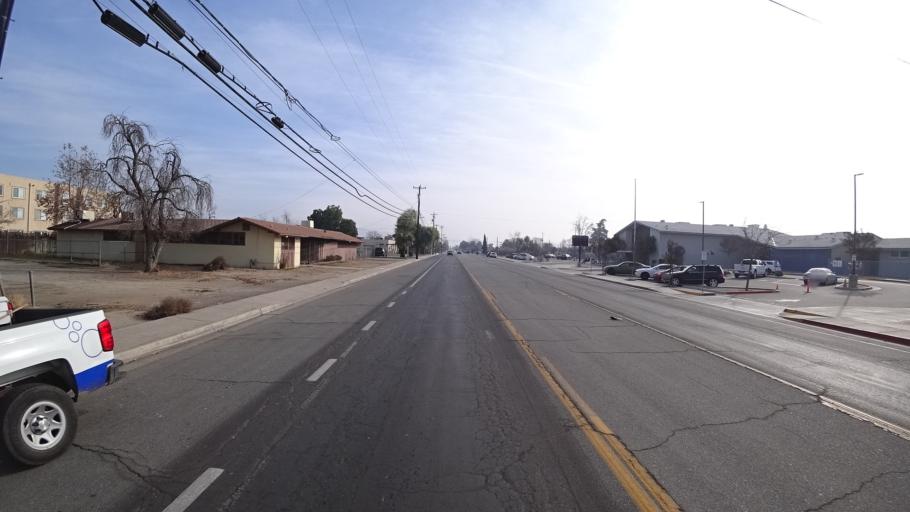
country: US
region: California
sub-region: Kern County
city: Bakersfield
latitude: 35.3608
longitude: -119.0092
